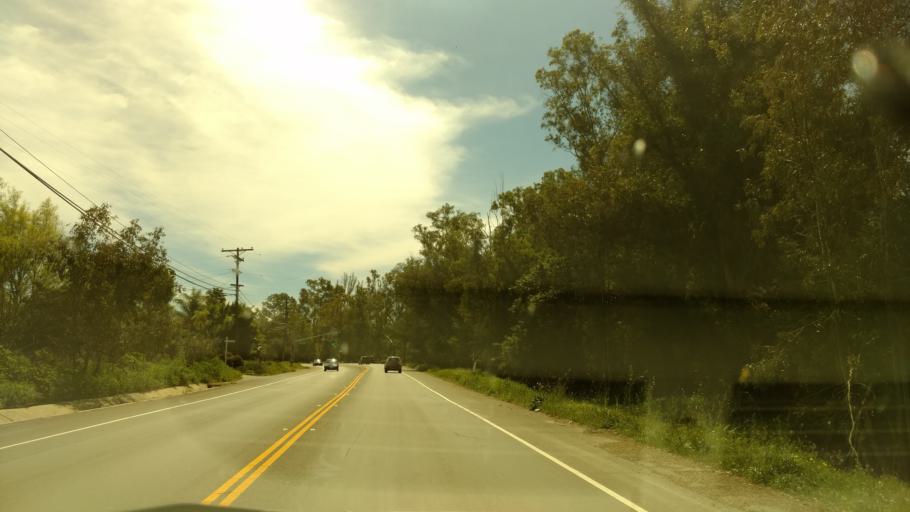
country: US
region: California
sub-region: San Diego County
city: Escondido
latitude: 33.1130
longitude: -117.0570
